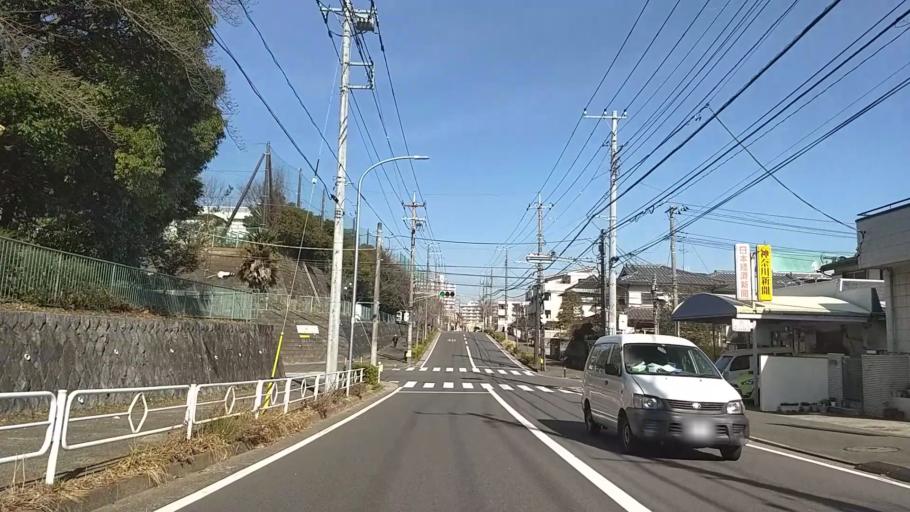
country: JP
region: Kanagawa
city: Kamakura
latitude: 35.3699
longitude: 139.5887
